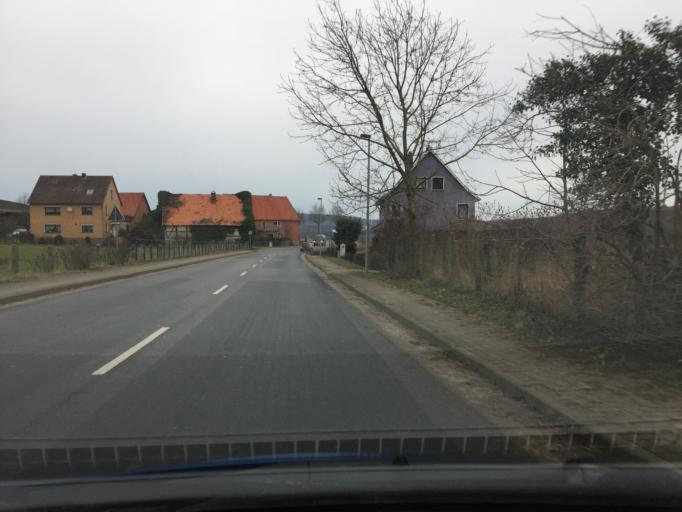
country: DE
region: Lower Saxony
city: Luerdissen
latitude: 51.9803
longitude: 9.6528
